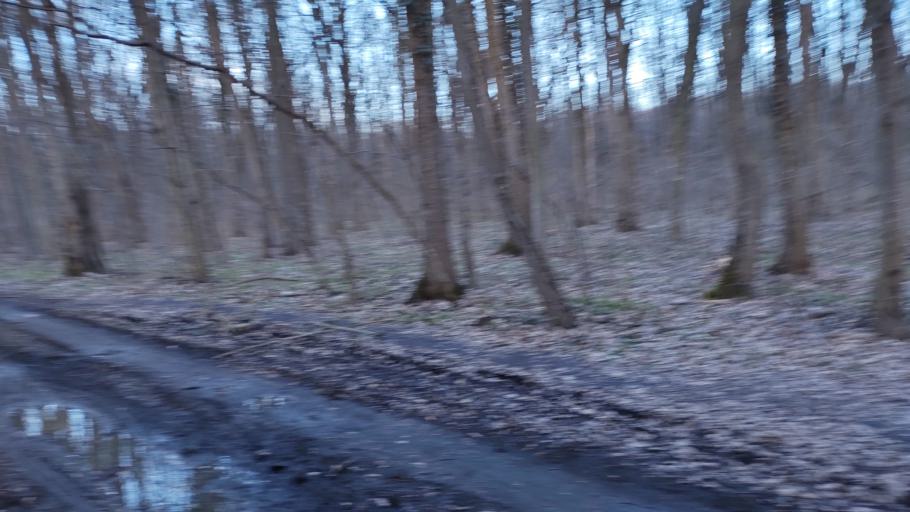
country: RO
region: Ilfov
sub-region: Comuna Otopeni
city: Otopeni
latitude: 44.5255
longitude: 26.0820
